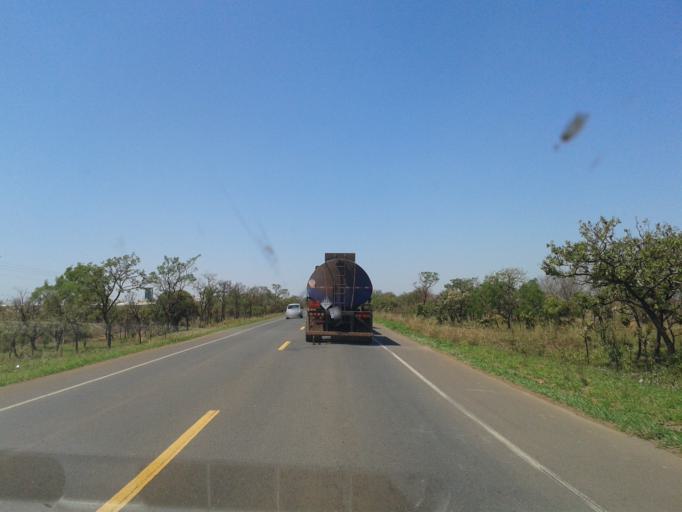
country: BR
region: Minas Gerais
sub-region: Araxa
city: Araxa
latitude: -19.3056
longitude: -47.3938
